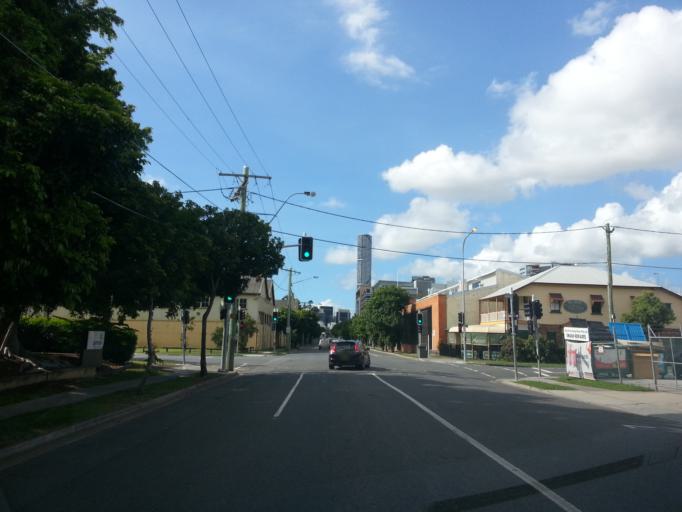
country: AU
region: Queensland
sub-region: Brisbane
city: Milton
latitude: -27.4760
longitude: 153.0091
